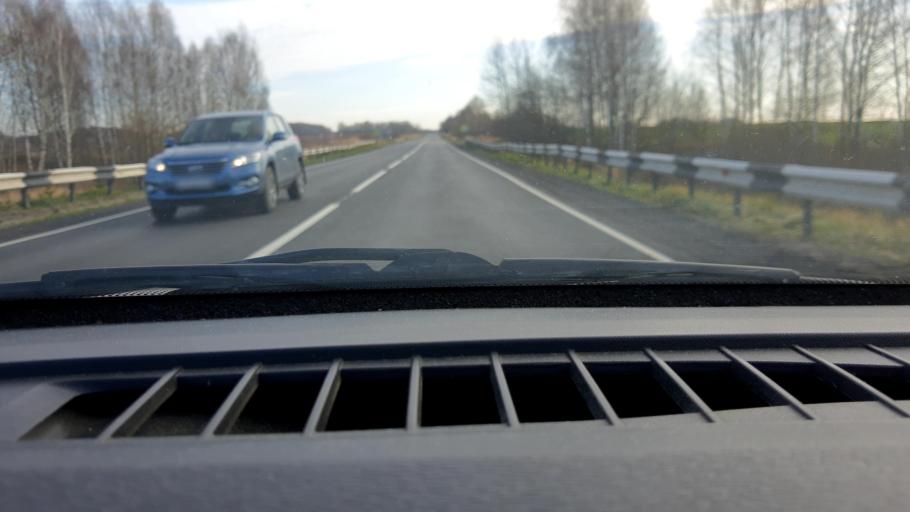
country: RU
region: Nizjnij Novgorod
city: Novaya Balakhna
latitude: 56.5827
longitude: 43.6820
